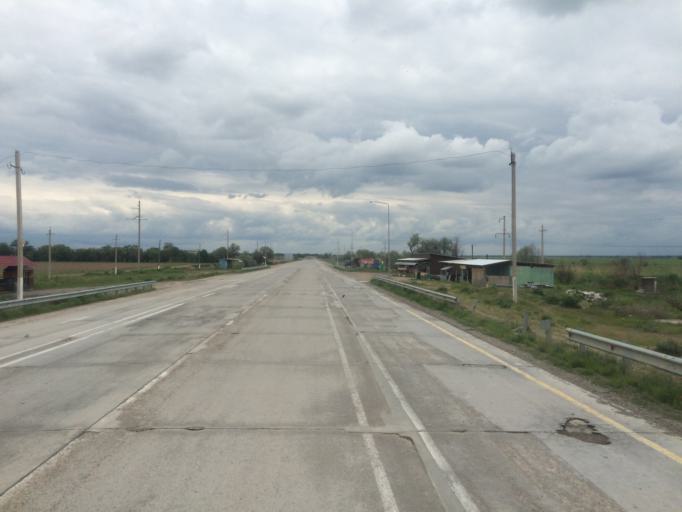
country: KG
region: Chuy
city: Sokuluk
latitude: 43.2720
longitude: 74.2382
